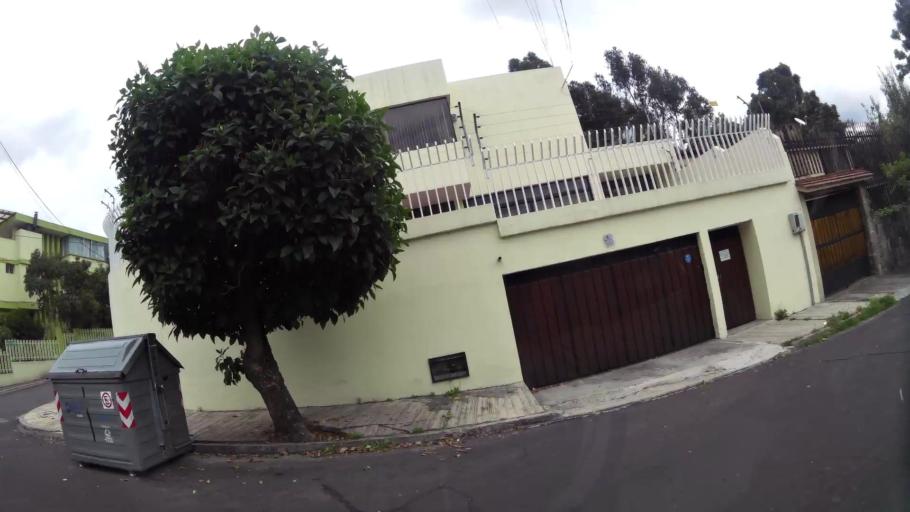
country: EC
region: Pichincha
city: Quito
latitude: -0.1817
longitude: -78.4967
